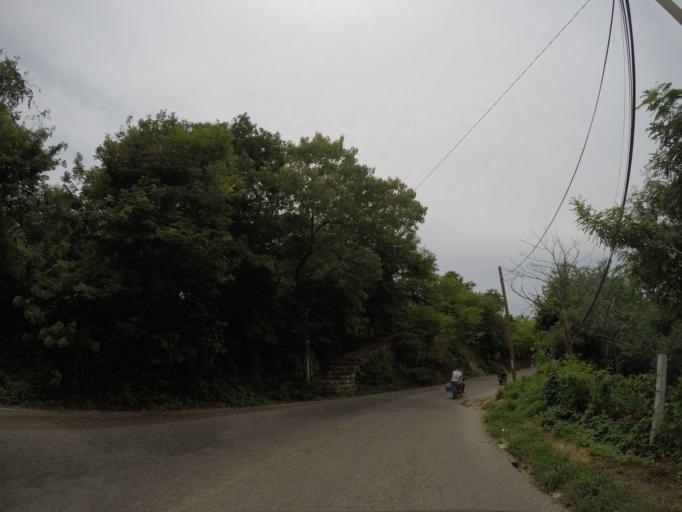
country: MX
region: Oaxaca
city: San Pedro Pochutla
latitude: 15.6682
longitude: -96.4964
